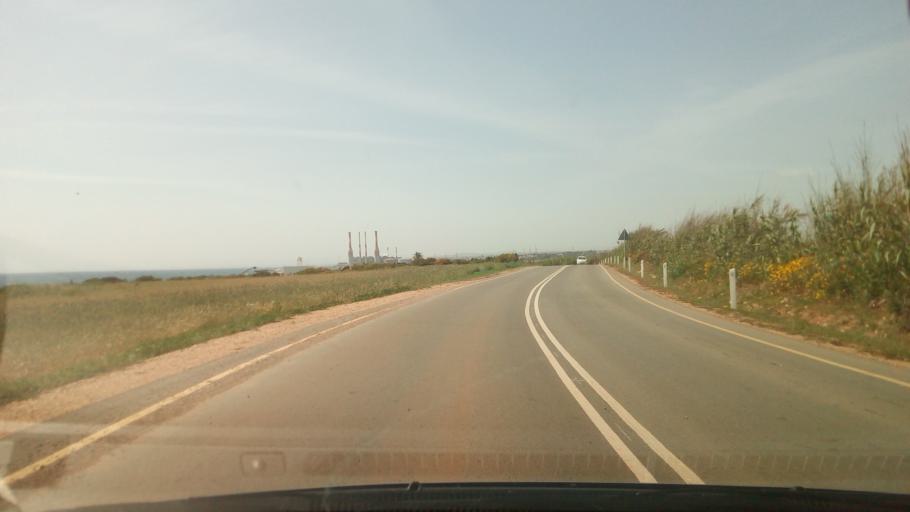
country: CY
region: Larnaka
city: Xylotymbou
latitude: 34.9810
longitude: 33.7690
